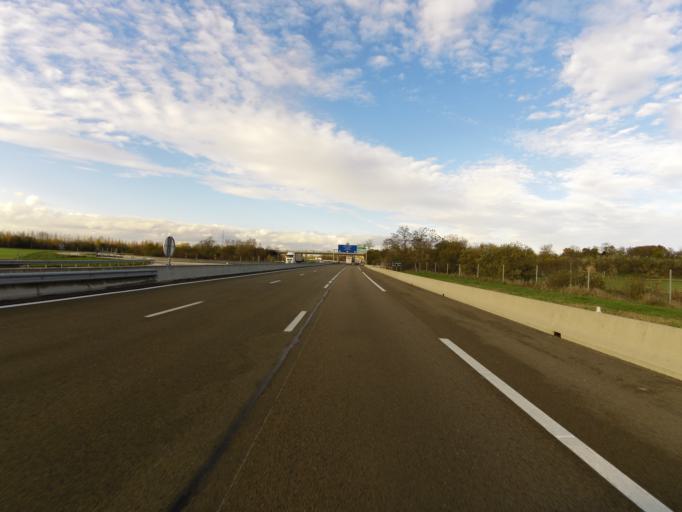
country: FR
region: Bourgogne
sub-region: Departement de la Cote-d'Or
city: Couternon
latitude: 47.3394
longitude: 5.1653
